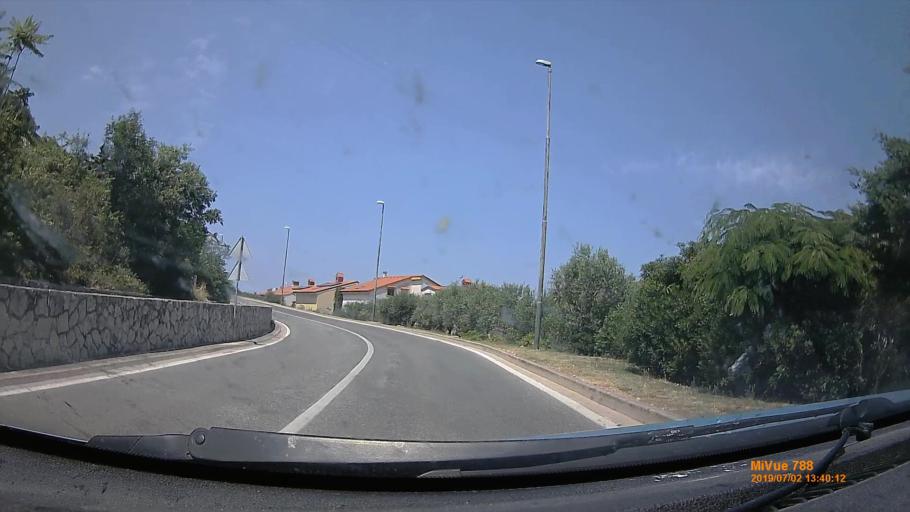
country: HR
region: Primorsko-Goranska
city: Mali Losinj
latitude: 44.5310
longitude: 14.4766
